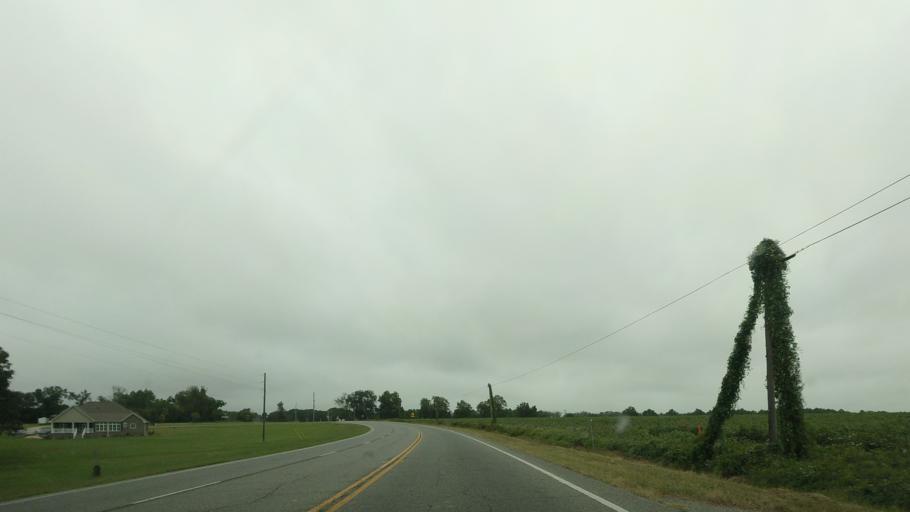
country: US
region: Georgia
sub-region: Ben Hill County
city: Fitzgerald
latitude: 31.6638
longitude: -83.2356
